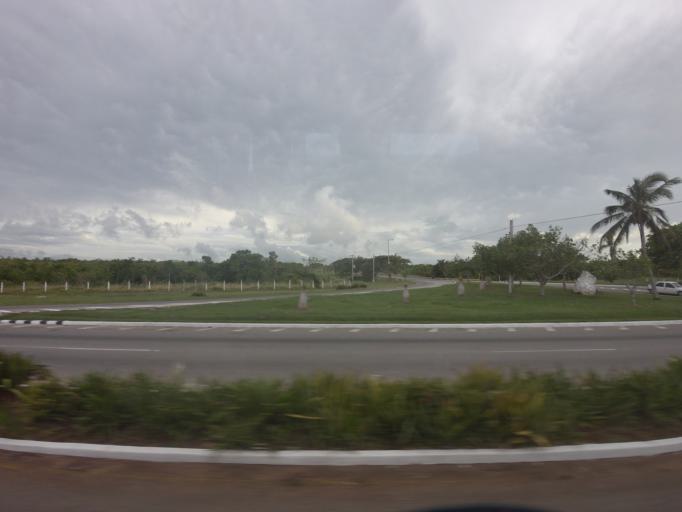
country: CU
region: Matanzas
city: Matanzas
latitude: 23.0808
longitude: -81.4414
